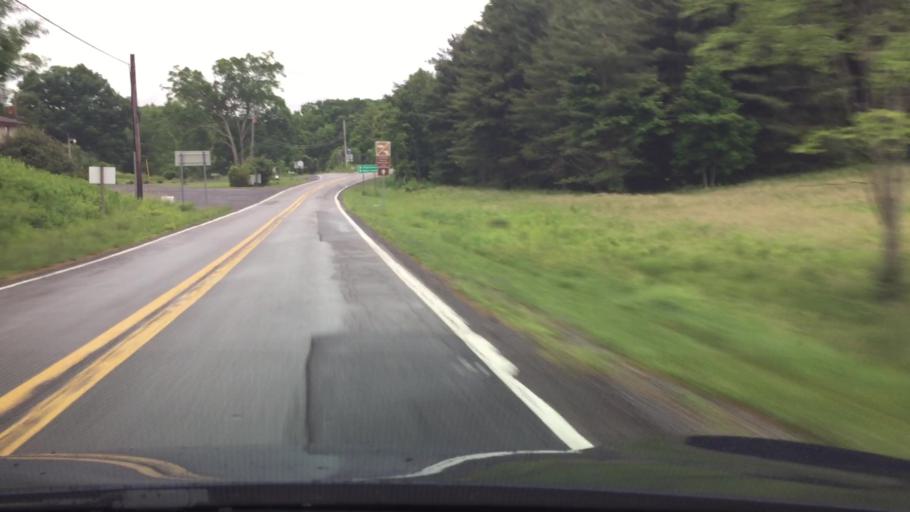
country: US
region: West Virginia
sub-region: Summers County
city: Hinton
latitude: 37.5683
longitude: -80.7900
